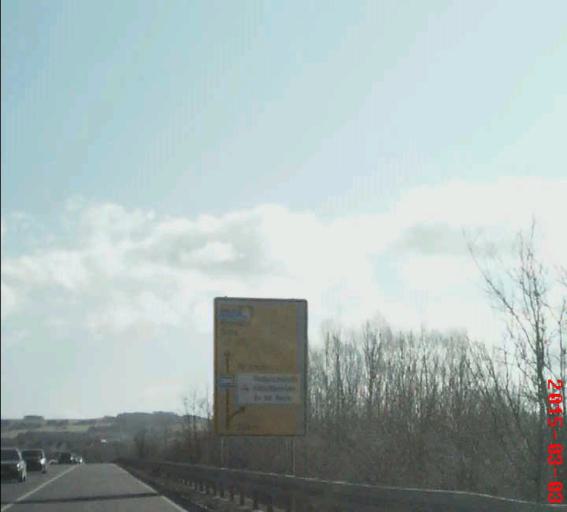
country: DE
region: Thuringia
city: Saalfeld
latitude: 50.6619
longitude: 11.3588
